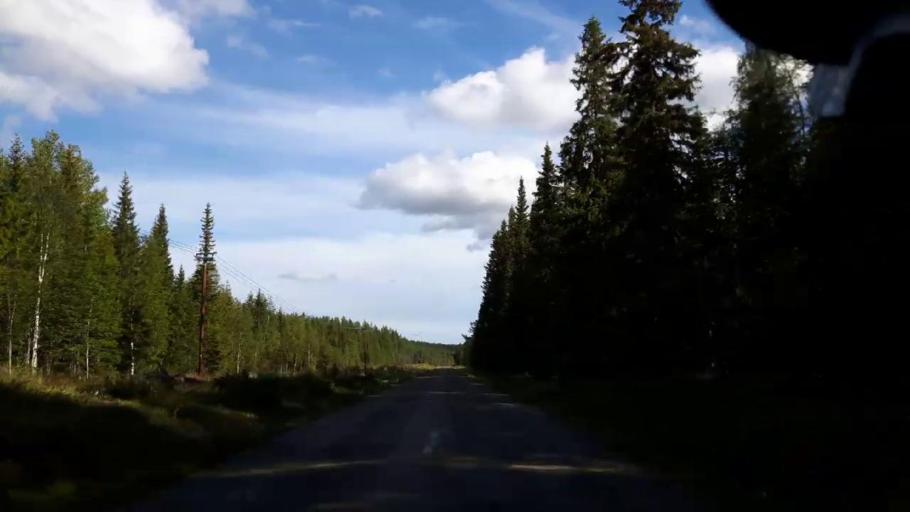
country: SE
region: Jaemtland
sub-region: Ragunda Kommun
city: Hammarstrand
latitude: 63.4315
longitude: 16.0434
